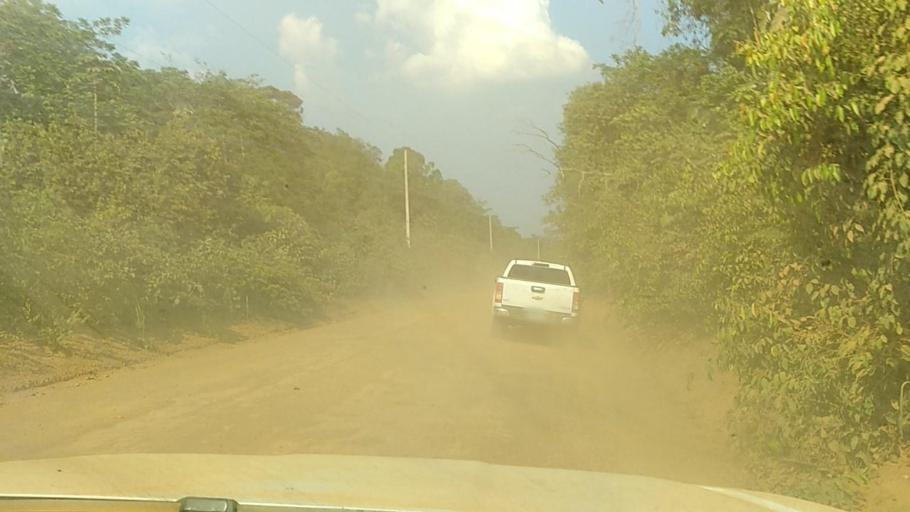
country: BR
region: Rondonia
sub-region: Porto Velho
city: Porto Velho
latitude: -8.6704
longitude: -64.0119
